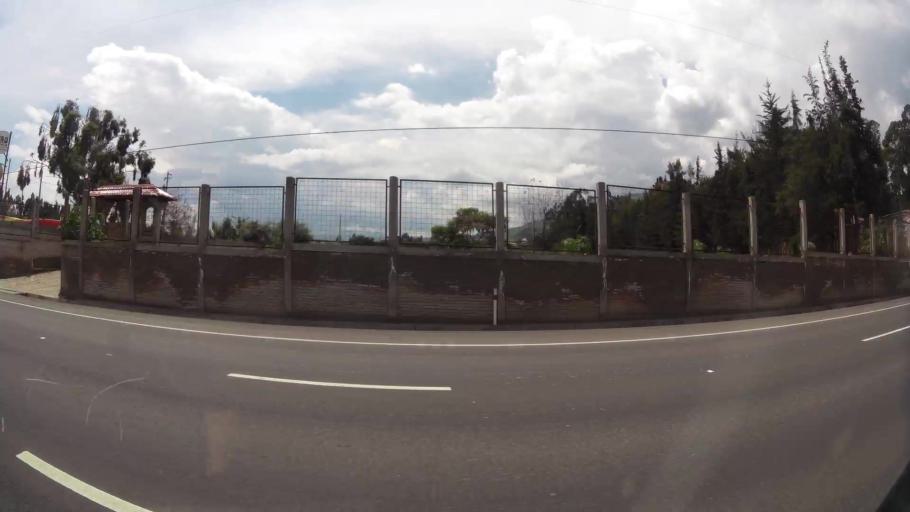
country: EC
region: Pichincha
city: Sangolqui
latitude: -0.2053
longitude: -78.3330
